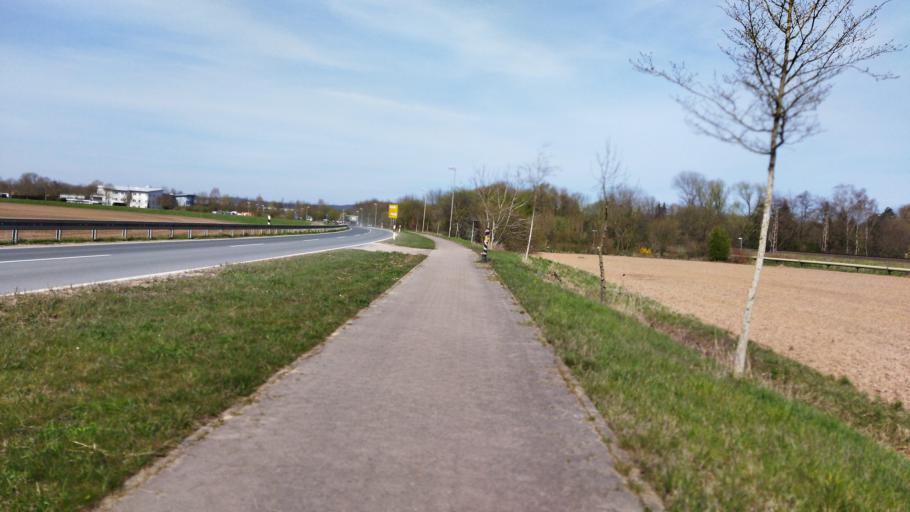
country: DE
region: Lower Saxony
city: Hameln
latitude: 52.0846
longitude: 9.3789
